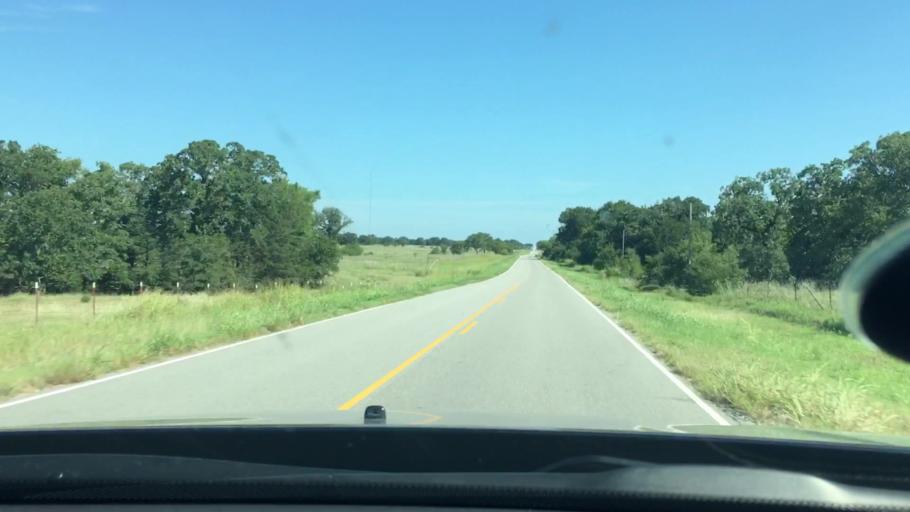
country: US
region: Oklahoma
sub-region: Johnston County
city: Tishomingo
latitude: 34.3125
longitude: -96.5487
